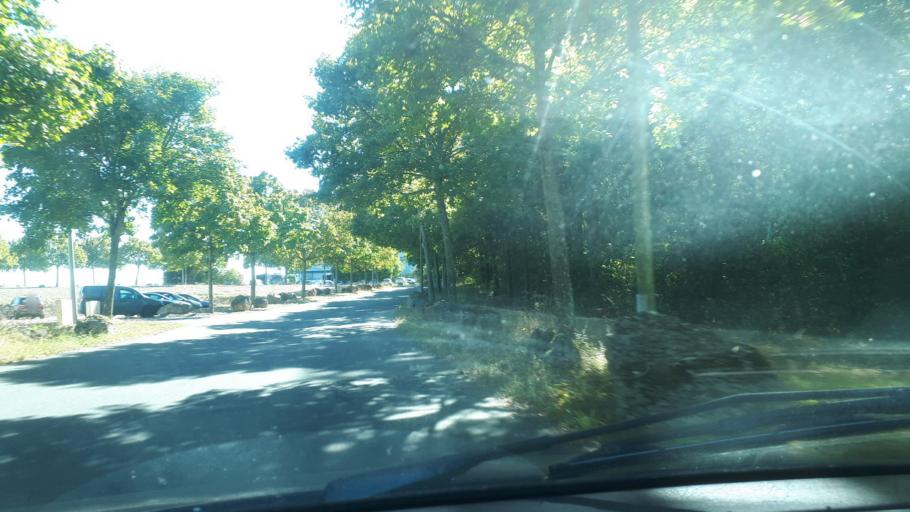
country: FR
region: Centre
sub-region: Departement du Loir-et-Cher
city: Naveil
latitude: 47.8135
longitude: 1.0254
